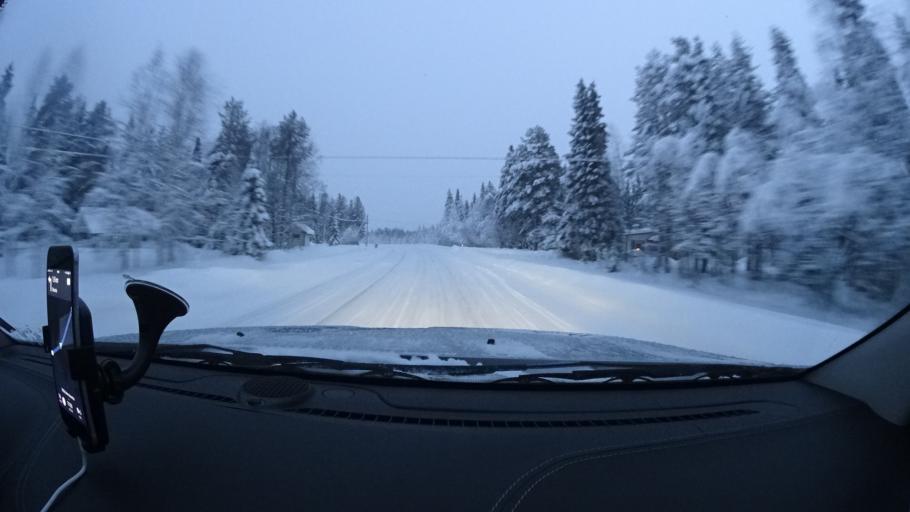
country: FI
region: Lapland
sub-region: Tunturi-Lappi
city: Kittilae
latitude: 67.6638
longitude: 24.8521
